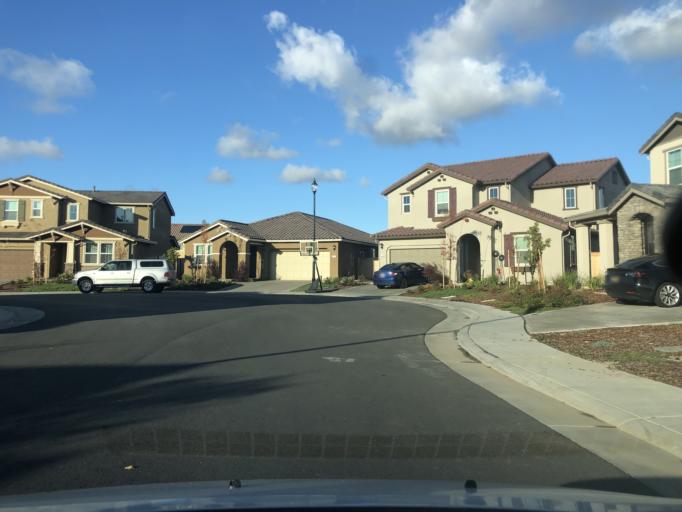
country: US
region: California
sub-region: Sacramento County
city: Antelope
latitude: 38.7714
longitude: -121.3774
